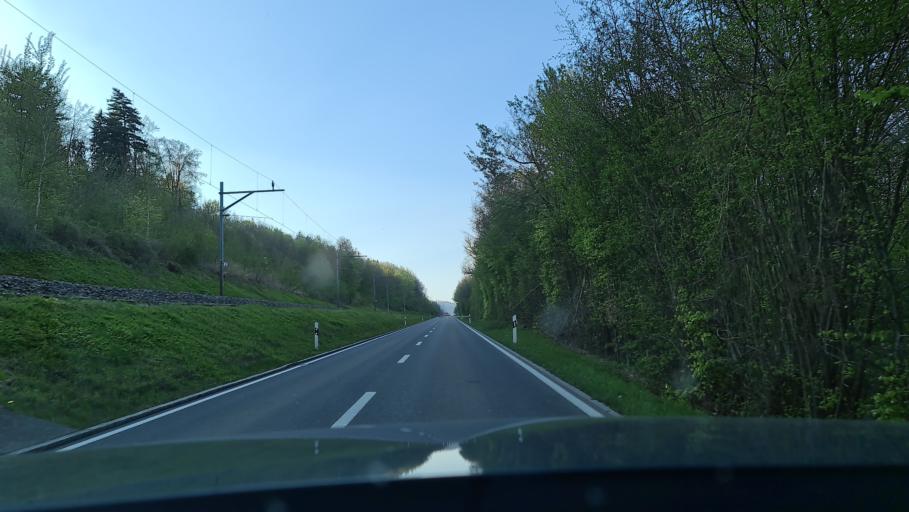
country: CH
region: Aargau
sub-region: Bezirk Kulm
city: Menziken
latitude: 47.2487
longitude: 8.2204
